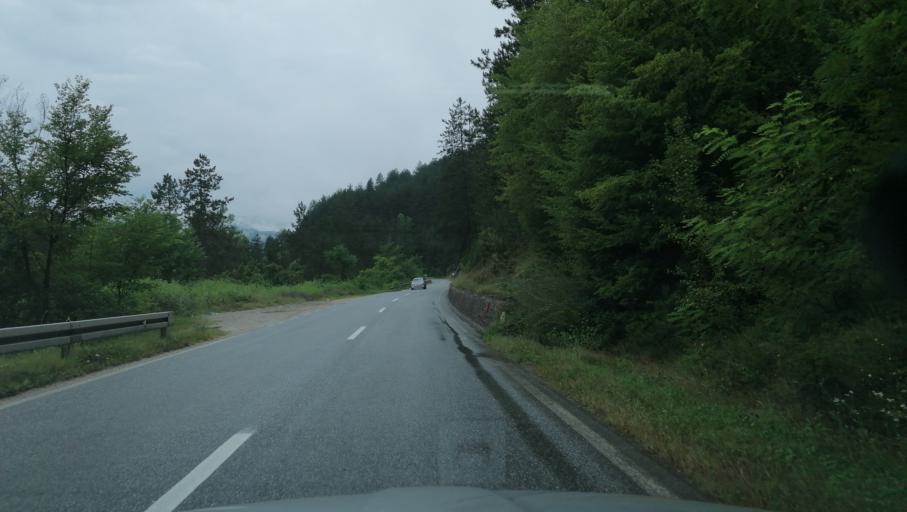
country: BA
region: Republika Srpska
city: Visegrad
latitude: 43.7843
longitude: 19.3211
